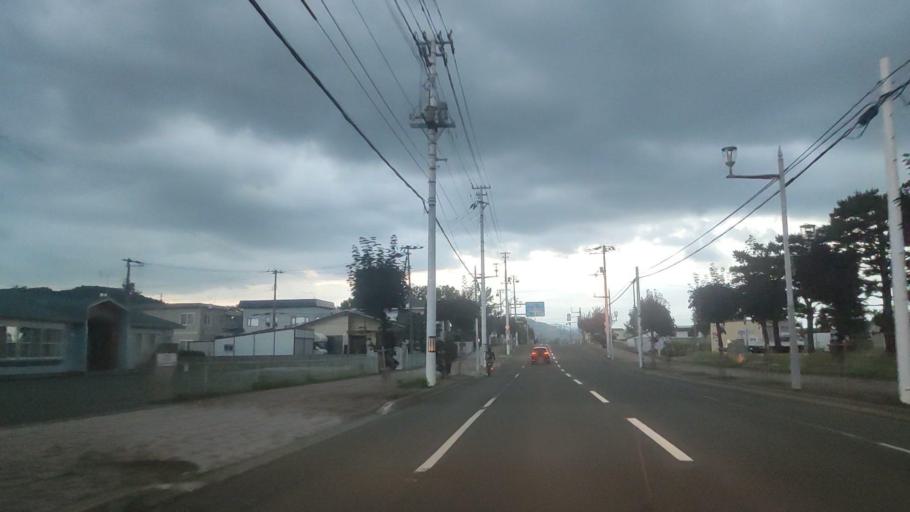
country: JP
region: Hokkaido
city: Shimo-furano
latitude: 43.3526
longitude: 142.3834
